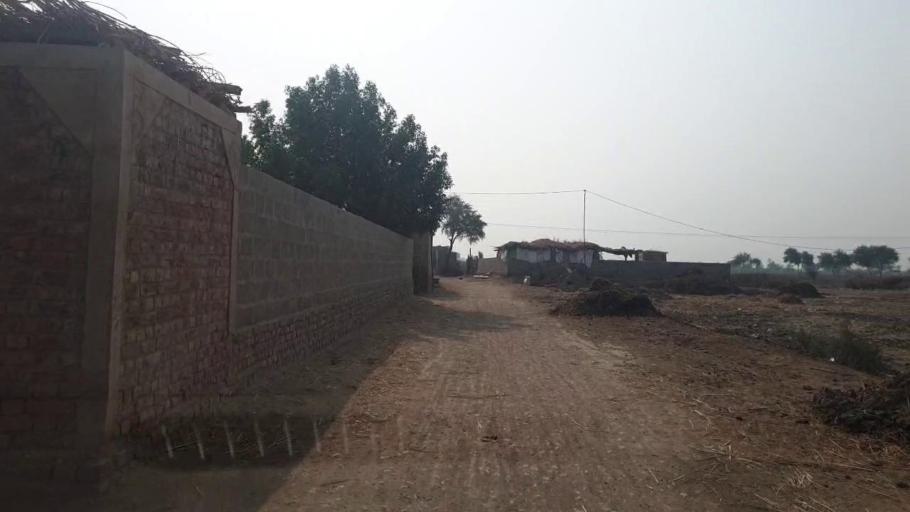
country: PK
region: Sindh
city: Tando Muhammad Khan
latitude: 25.2749
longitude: 68.4893
